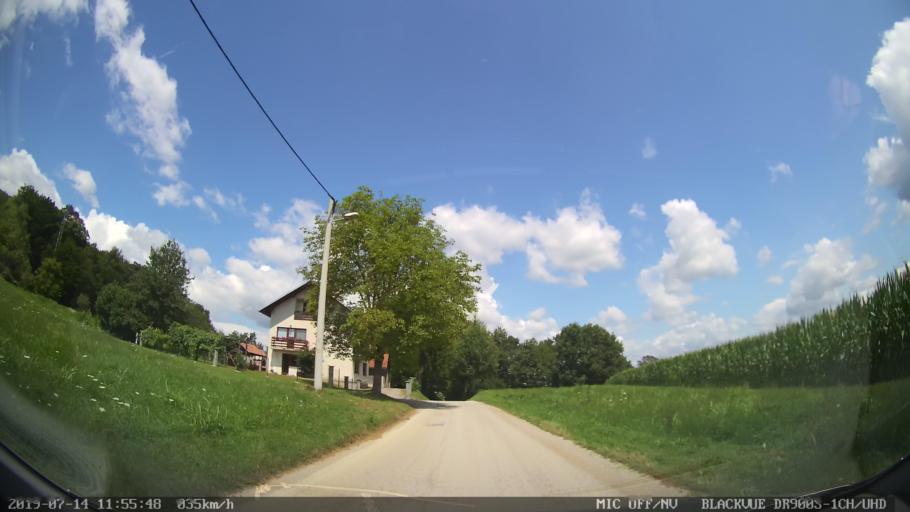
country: HR
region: Karlovacka
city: Vojnic
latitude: 45.3843
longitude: 15.6070
